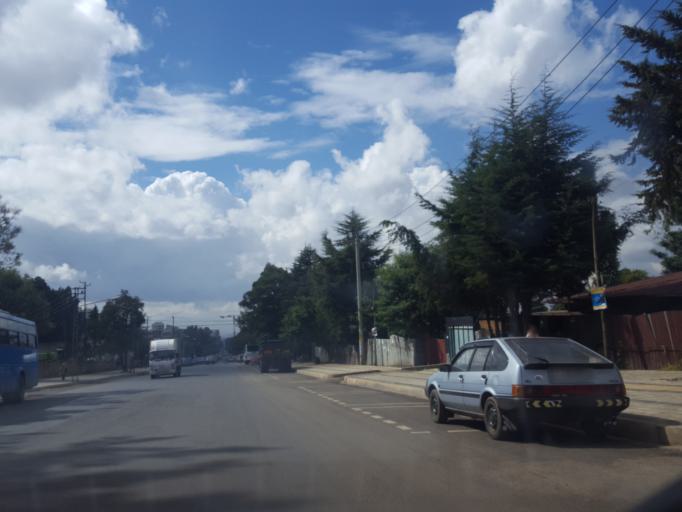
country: ET
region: Adis Abeba
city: Addis Ababa
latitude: 9.0554
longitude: 38.7626
